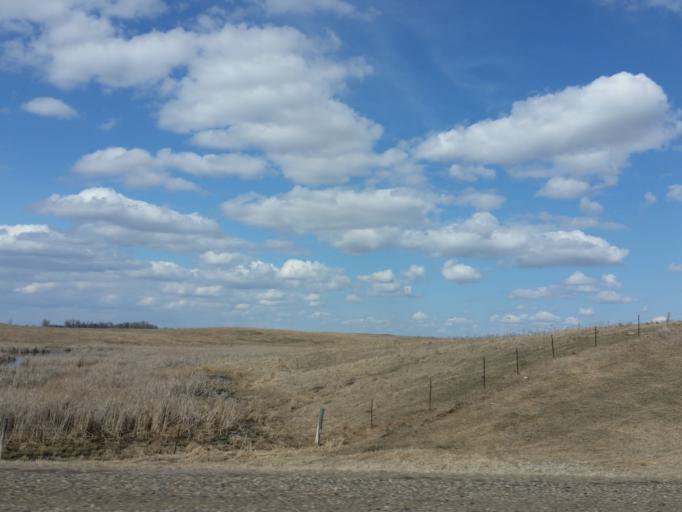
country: US
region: South Dakota
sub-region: Deuel County
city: Clear Lake
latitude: 44.8901
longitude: -96.7728
